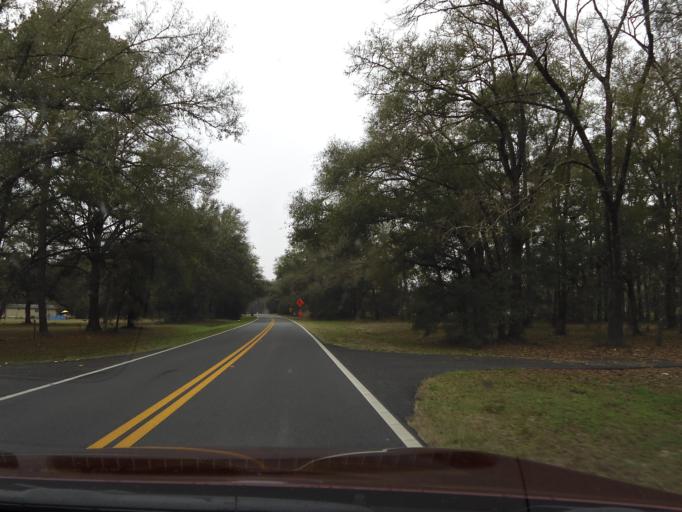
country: US
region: Florida
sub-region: Alachua County
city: High Springs
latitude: 29.8494
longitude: -82.5827
